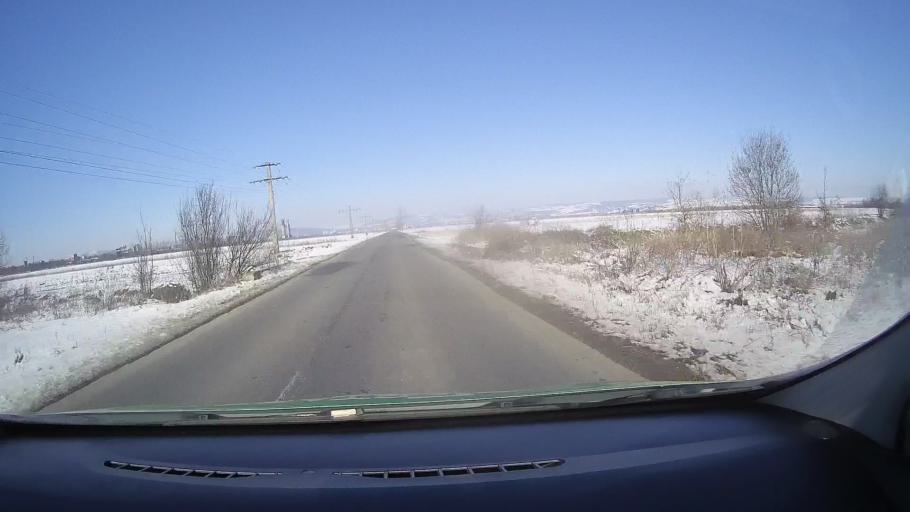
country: RO
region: Brasov
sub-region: Comuna Harseni
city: Harseni
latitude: 45.7974
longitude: 24.9941
